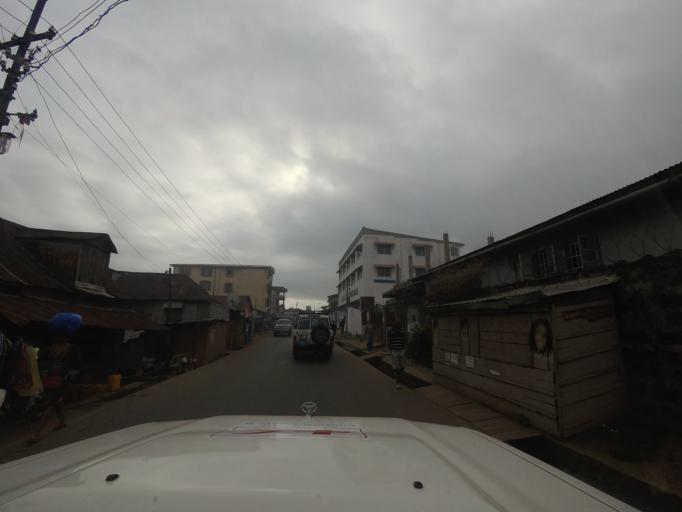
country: SL
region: Western Area
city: Freetown
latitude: 8.4843
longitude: -13.2471
